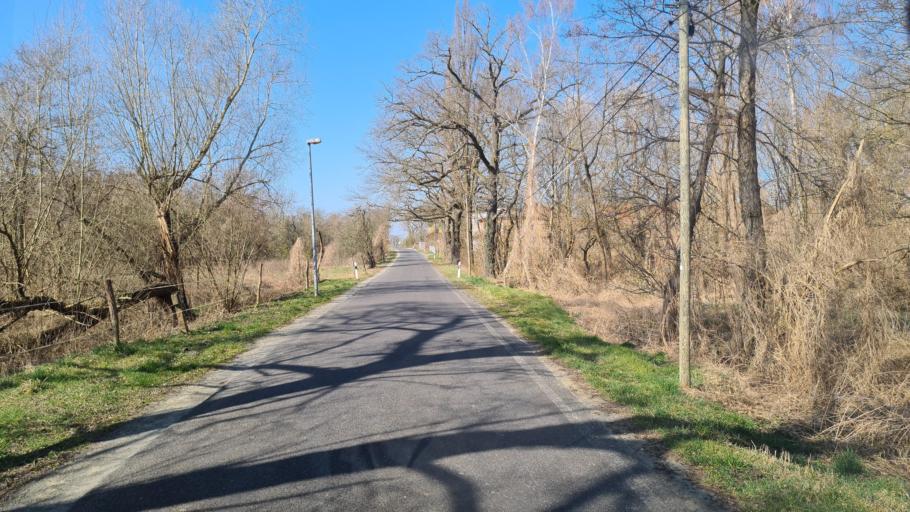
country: DE
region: Brandenburg
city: Vetschau
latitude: 51.7866
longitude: 14.0410
